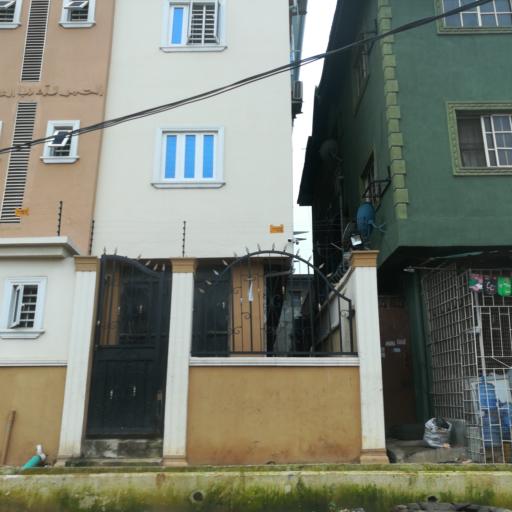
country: NG
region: Lagos
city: Ebute Metta
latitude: 6.4872
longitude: 3.3865
